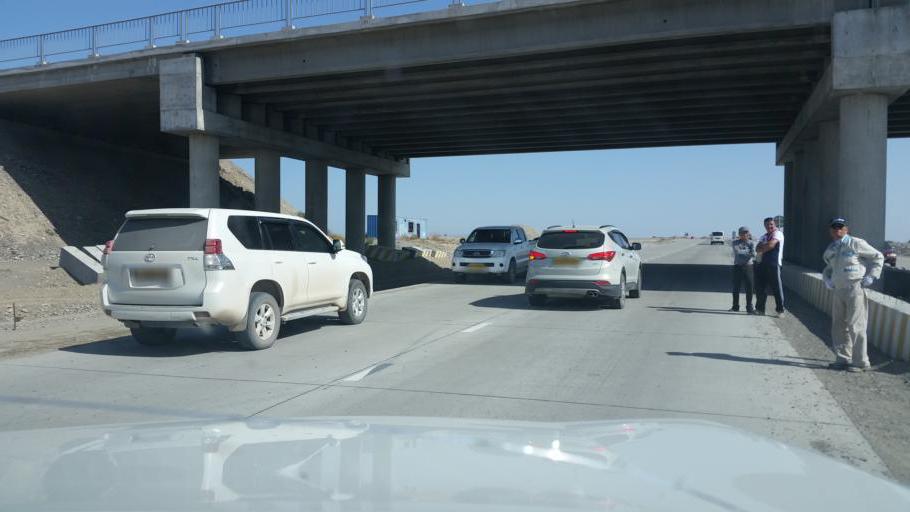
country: KZ
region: Almaty Oblysy
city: Turgen'
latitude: 43.6051
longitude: 78.3115
